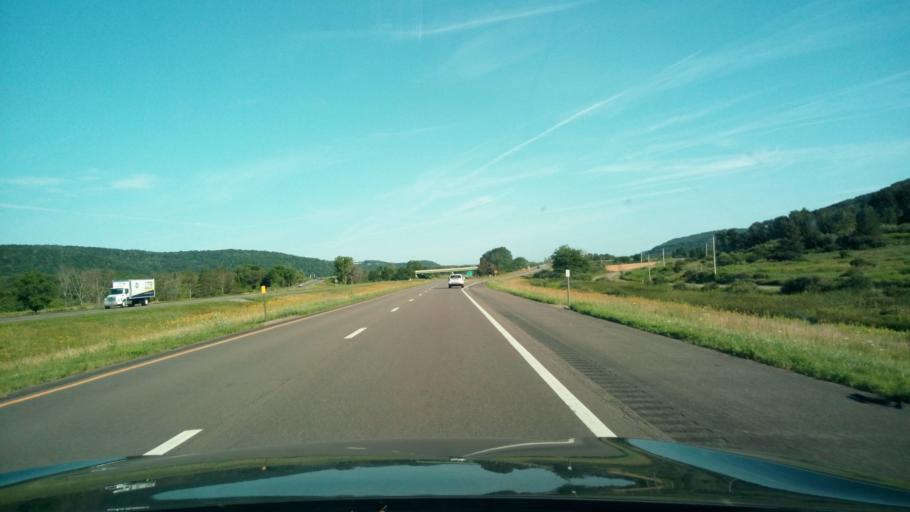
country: US
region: New York
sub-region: Steuben County
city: Bath
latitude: 42.3974
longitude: -77.4003
